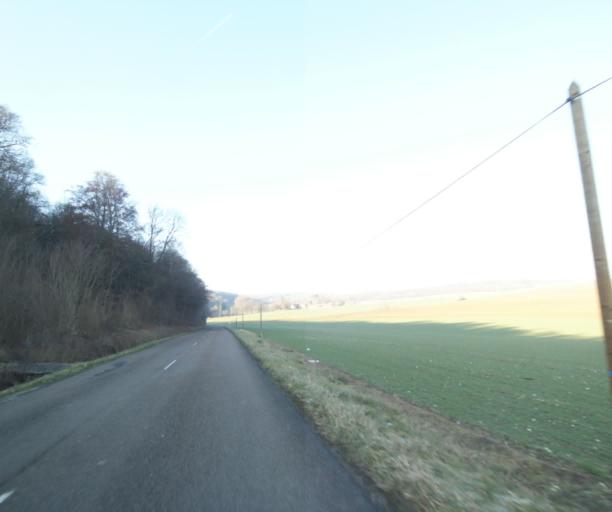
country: FR
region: Champagne-Ardenne
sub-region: Departement de la Haute-Marne
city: Chevillon
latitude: 48.5519
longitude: 5.0926
